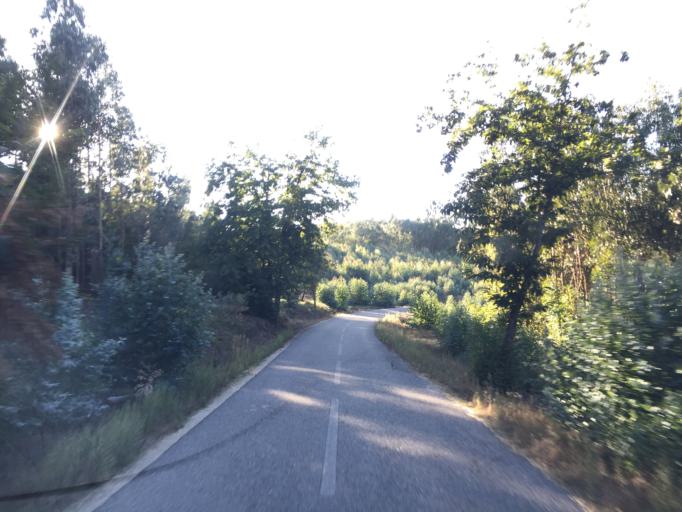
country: PT
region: Portalegre
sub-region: Castelo de Vide
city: Castelo de Vide
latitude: 39.4041
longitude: -7.4569
